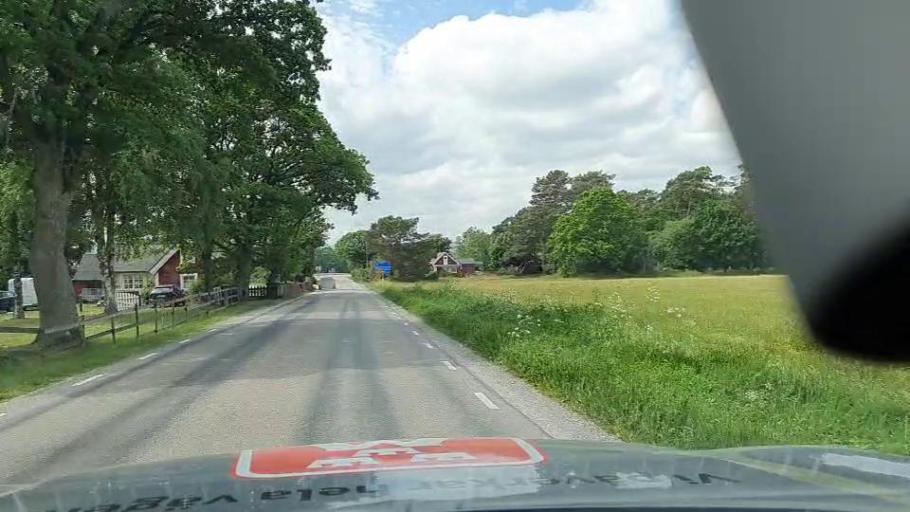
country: SE
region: Blekinge
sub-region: Karlshamns Kommun
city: Morrum
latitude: 56.1115
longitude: 14.6789
